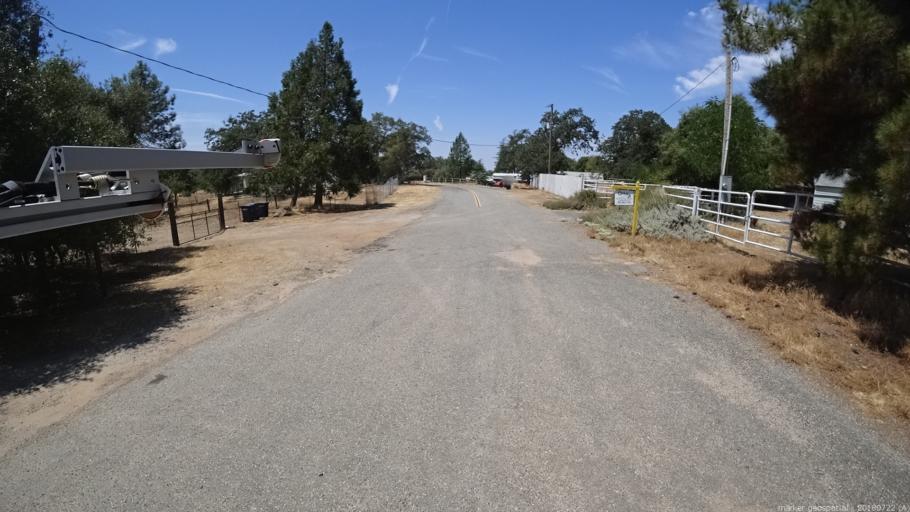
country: US
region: California
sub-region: Madera County
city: Coarsegold
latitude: 37.2587
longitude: -119.7330
